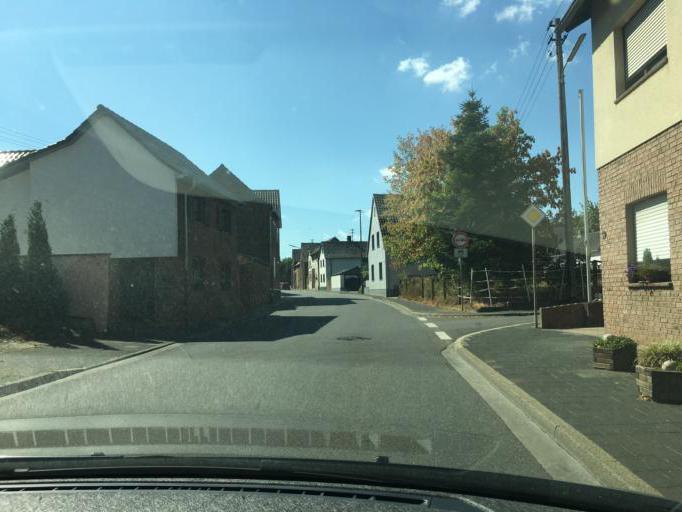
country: DE
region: North Rhine-Westphalia
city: Zulpich
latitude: 50.6752
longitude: 6.6156
